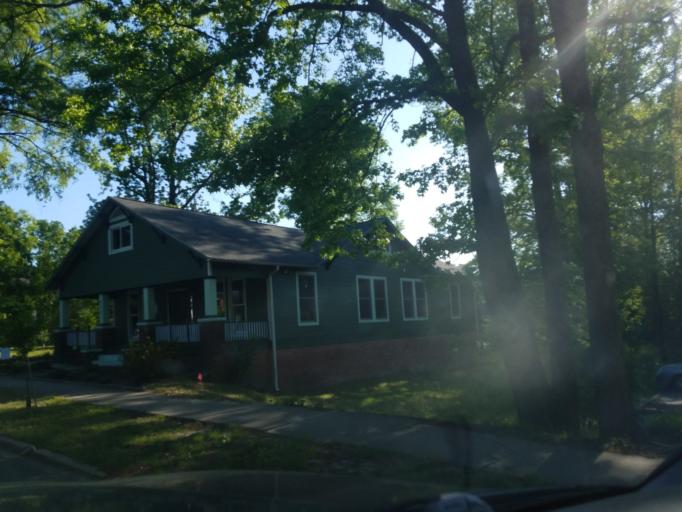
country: US
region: North Carolina
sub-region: Durham County
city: Durham
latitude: 36.0122
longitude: -78.9195
